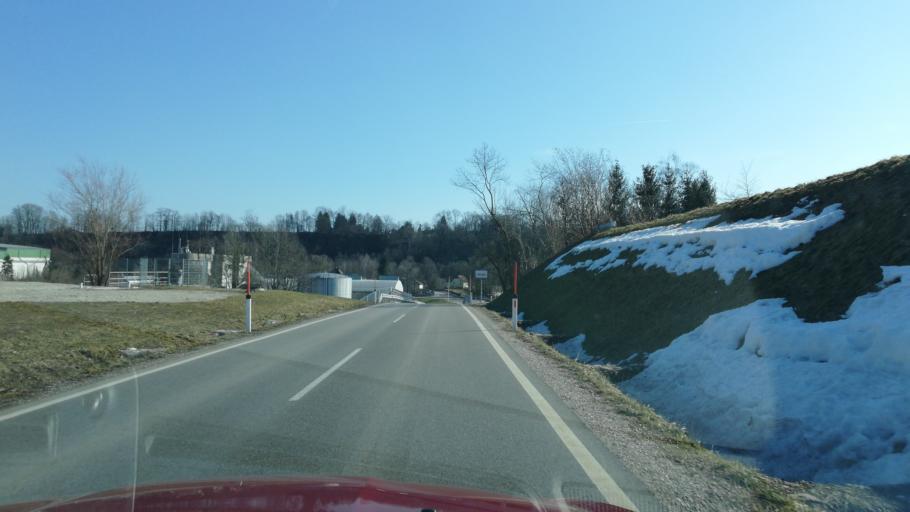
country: AT
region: Upper Austria
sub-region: Politischer Bezirk Vocklabruck
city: Redlham
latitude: 48.0156
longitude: 13.7445
